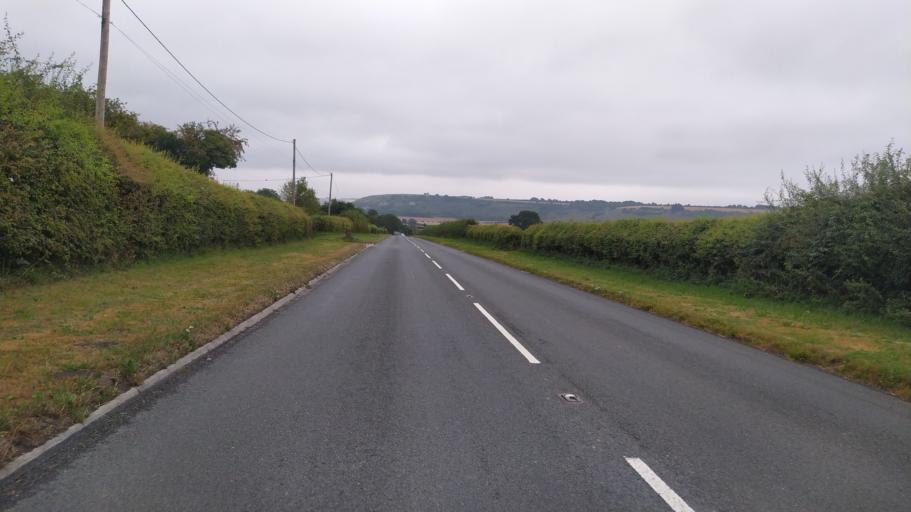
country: GB
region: England
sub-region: Wiltshire
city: Dinton
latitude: 51.0510
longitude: -2.0184
